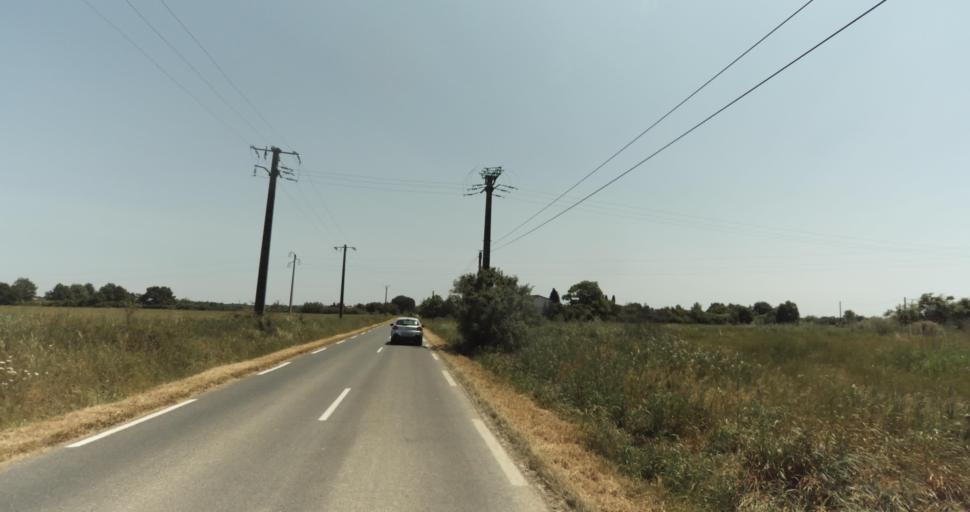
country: FR
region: Midi-Pyrenees
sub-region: Departement de la Haute-Garonne
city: La Salvetat-Saint-Gilles
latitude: 43.5897
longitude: 1.2535
